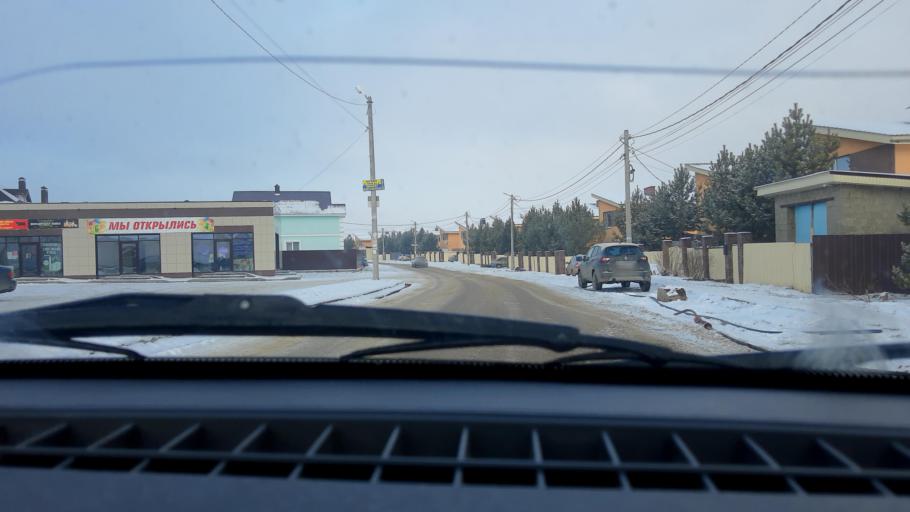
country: RU
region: Bashkortostan
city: Avdon
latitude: 54.4773
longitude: 55.8771
